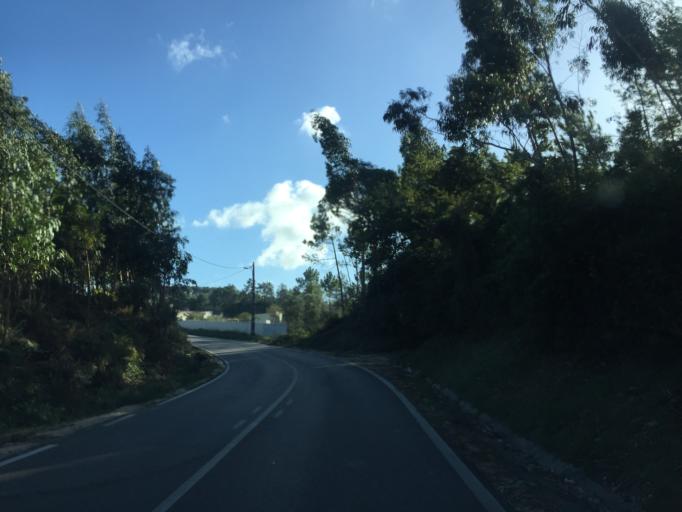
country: PT
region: Coimbra
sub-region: Figueira da Foz
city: Tavarede
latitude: 40.2000
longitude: -8.8355
